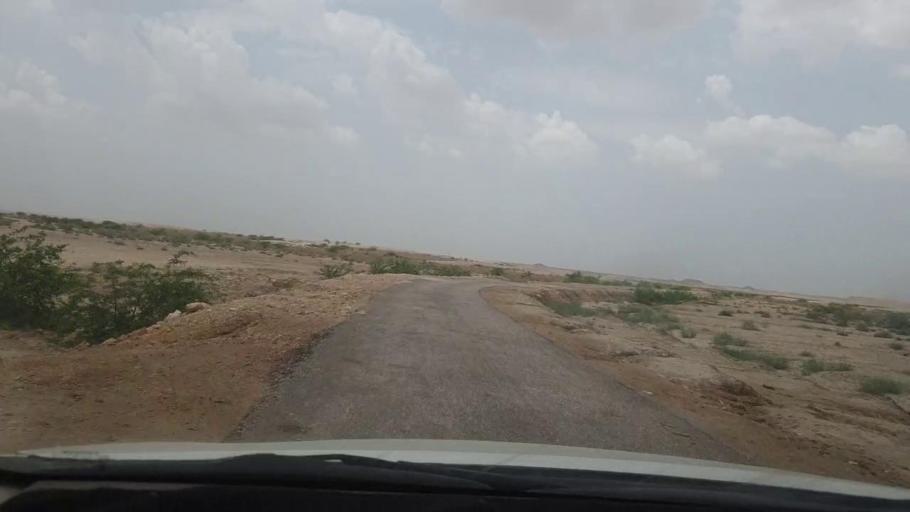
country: PK
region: Sindh
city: Khairpur
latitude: 27.3986
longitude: 68.9729
